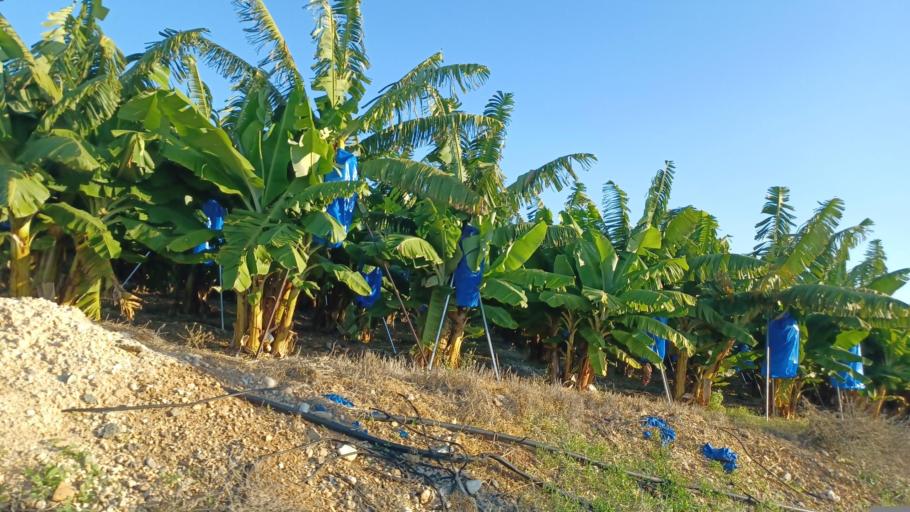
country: CY
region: Pafos
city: Pegeia
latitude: 34.8785
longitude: 32.3427
